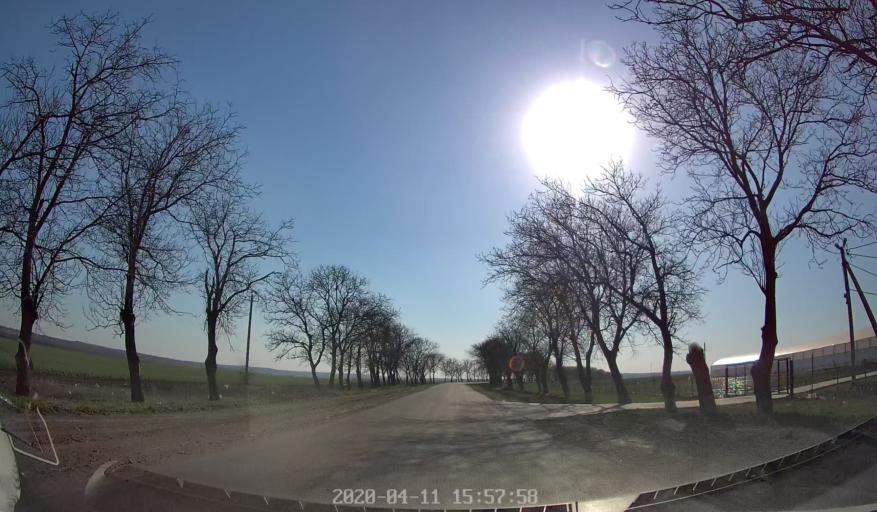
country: MD
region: Chisinau
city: Vadul lui Voda
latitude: 47.0867
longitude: 29.1630
